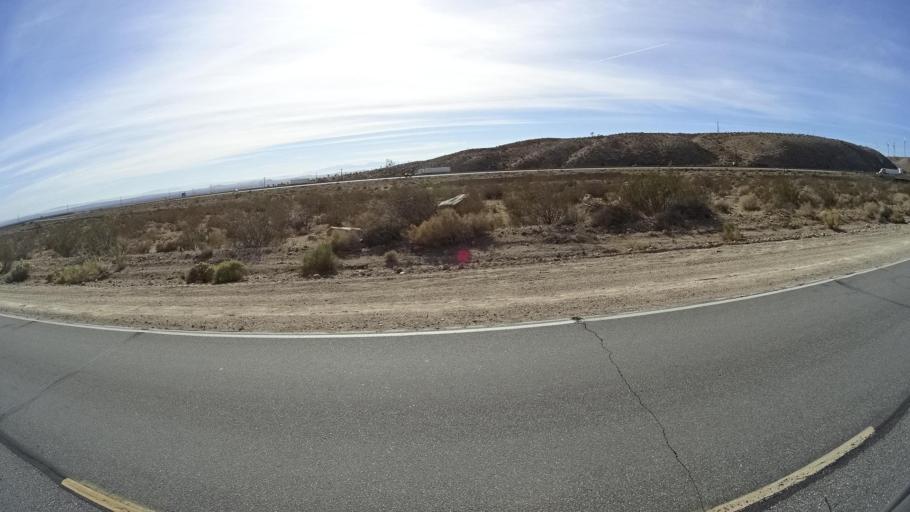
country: US
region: California
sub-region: Kern County
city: Mojave
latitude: 35.1190
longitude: -118.1984
